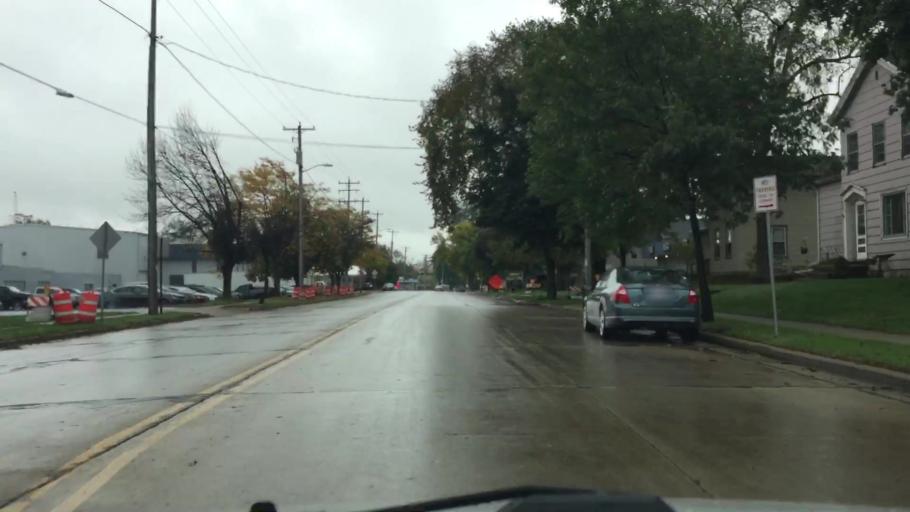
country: US
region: Wisconsin
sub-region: Walworth County
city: Whitewater
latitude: 42.8325
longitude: -88.7173
